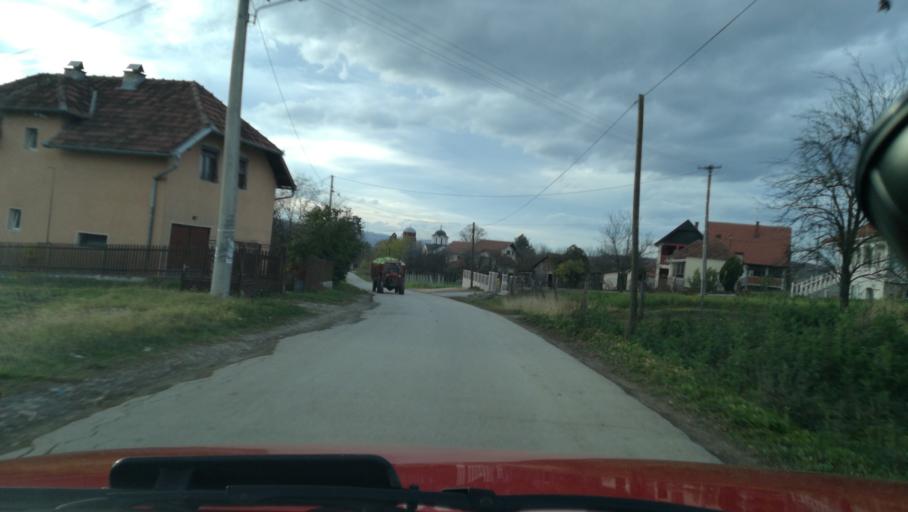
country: RS
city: Prislonica
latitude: 43.9154
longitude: 20.4115
